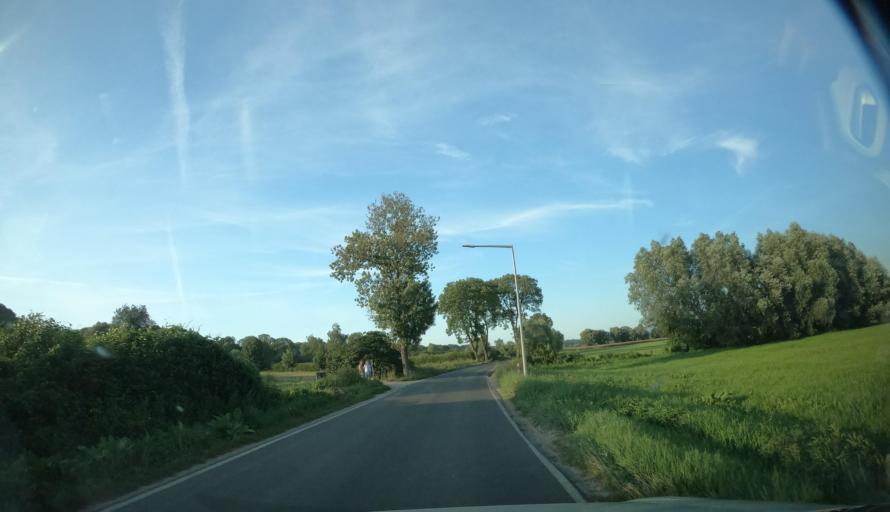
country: PL
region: Kujawsko-Pomorskie
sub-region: Bydgoszcz
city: Fordon
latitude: 53.2154
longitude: 18.1827
